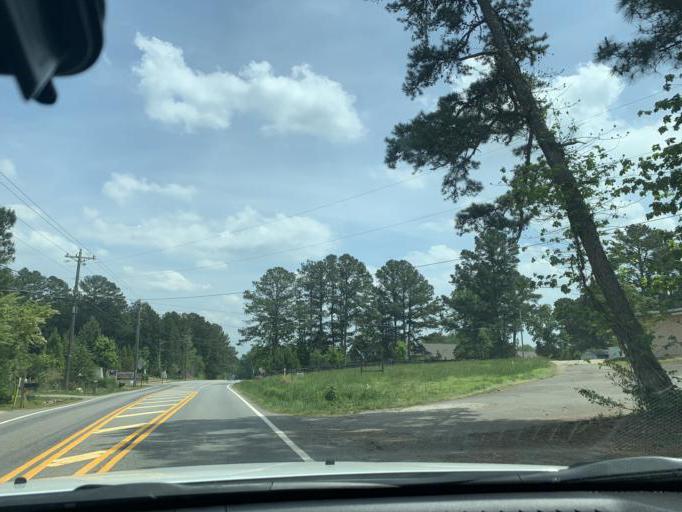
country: US
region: Georgia
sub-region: Forsyth County
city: Cumming
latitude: 34.1495
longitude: -84.1430
